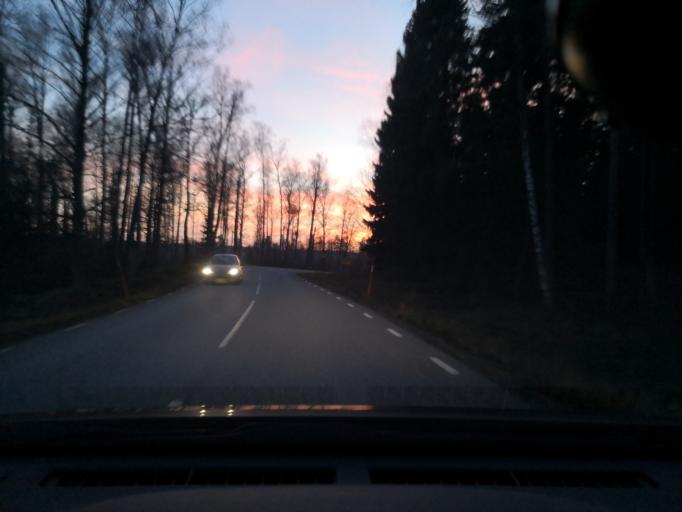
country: SE
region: OErebro
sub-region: Lindesbergs Kommun
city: Fellingsbro
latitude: 59.4041
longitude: 15.5305
